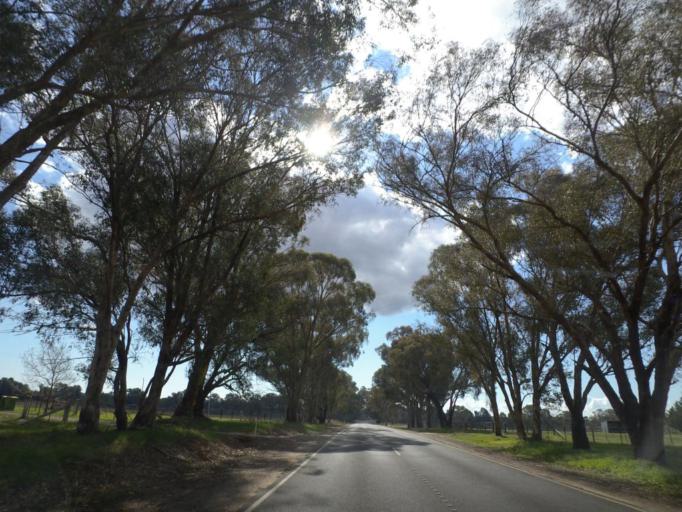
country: AU
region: New South Wales
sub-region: Corowa Shire
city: Howlong
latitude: -36.1662
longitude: 146.6073
